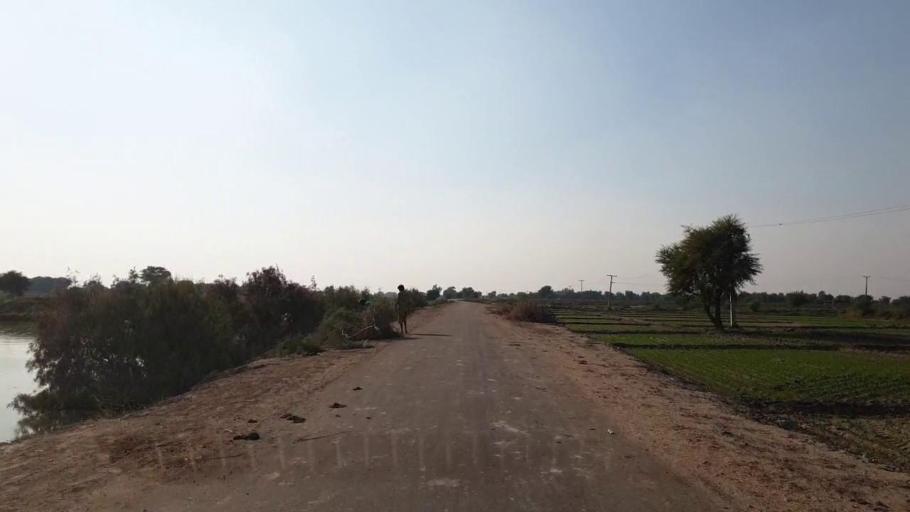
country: PK
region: Sindh
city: Sehwan
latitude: 26.4379
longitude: 67.7977
